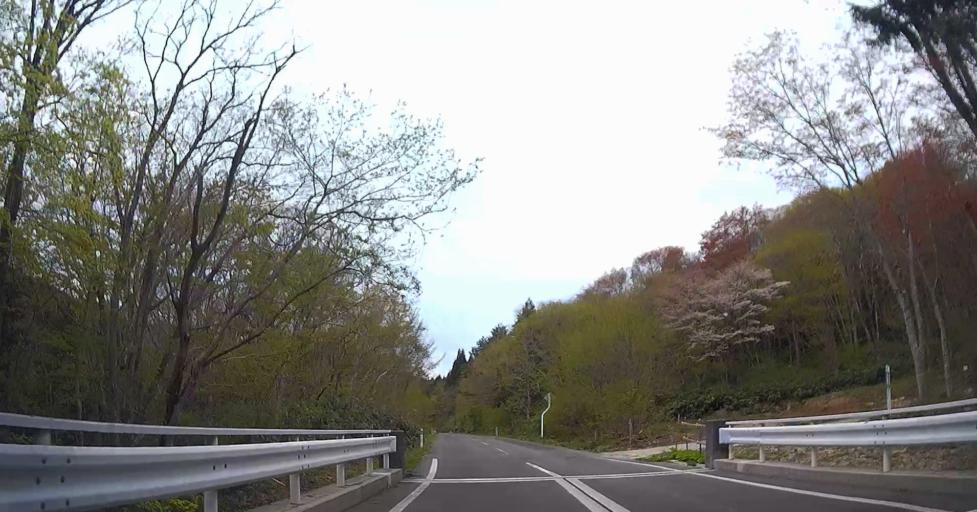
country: JP
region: Aomori
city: Goshogawara
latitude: 40.9038
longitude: 140.5292
